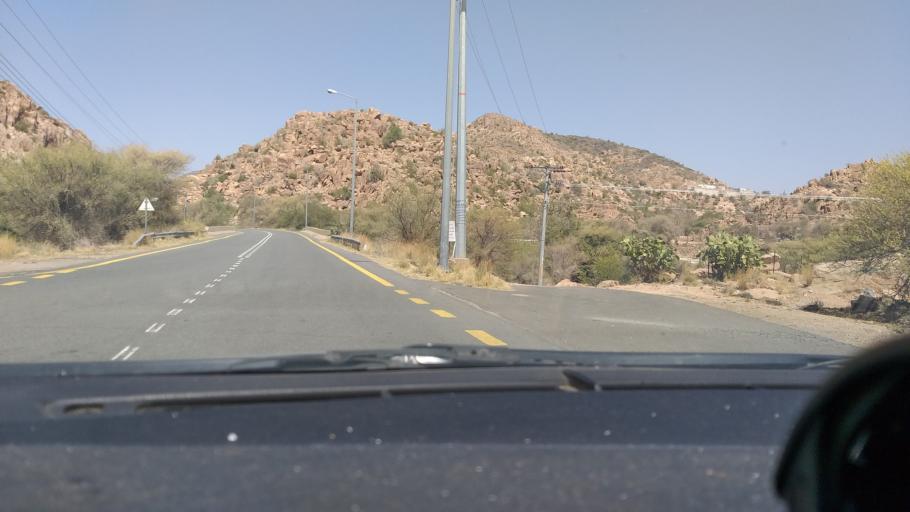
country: SA
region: Makkah
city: Ash Shafa
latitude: 21.0920
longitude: 40.3695
